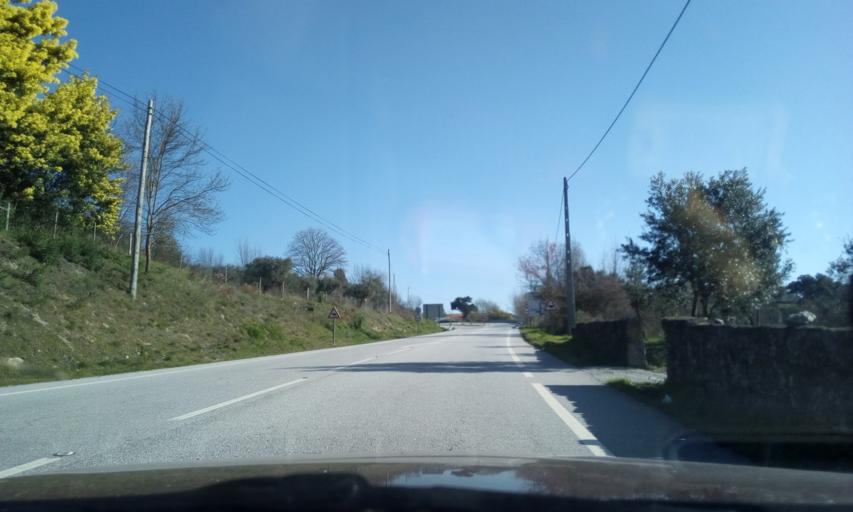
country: PT
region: Guarda
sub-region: Fornos de Algodres
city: Fornos de Algodres
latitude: 40.6241
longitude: -7.5074
